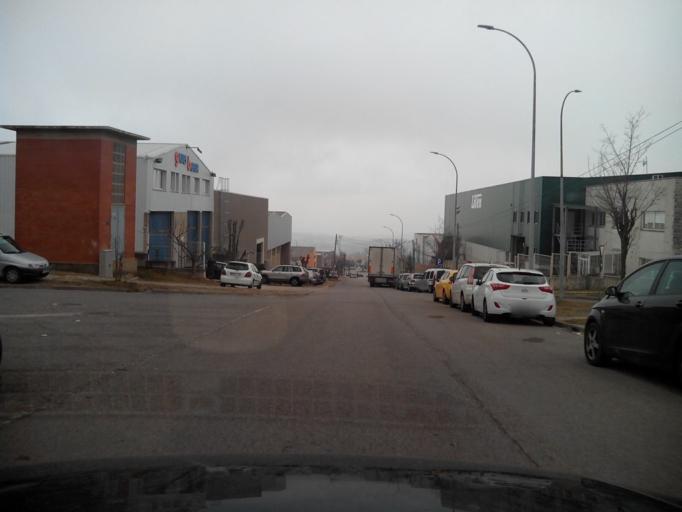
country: ES
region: Catalonia
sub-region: Provincia de Barcelona
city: Berga
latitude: 42.0951
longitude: 1.8217
